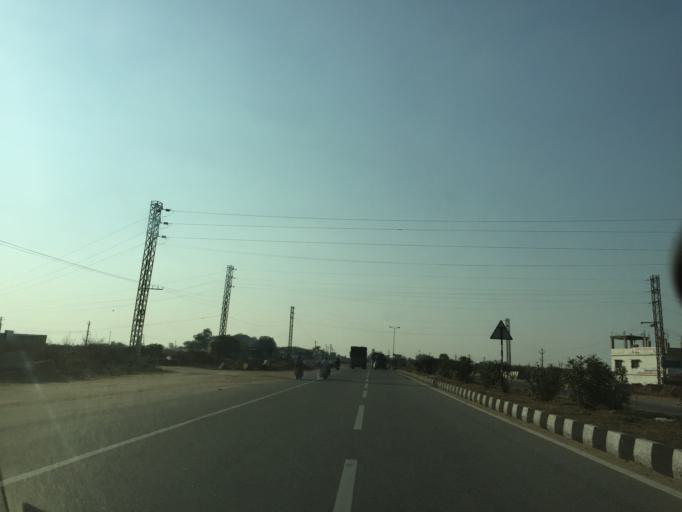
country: IN
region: Telangana
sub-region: Nalgonda
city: Bhongir
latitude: 17.5032
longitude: 78.8741
